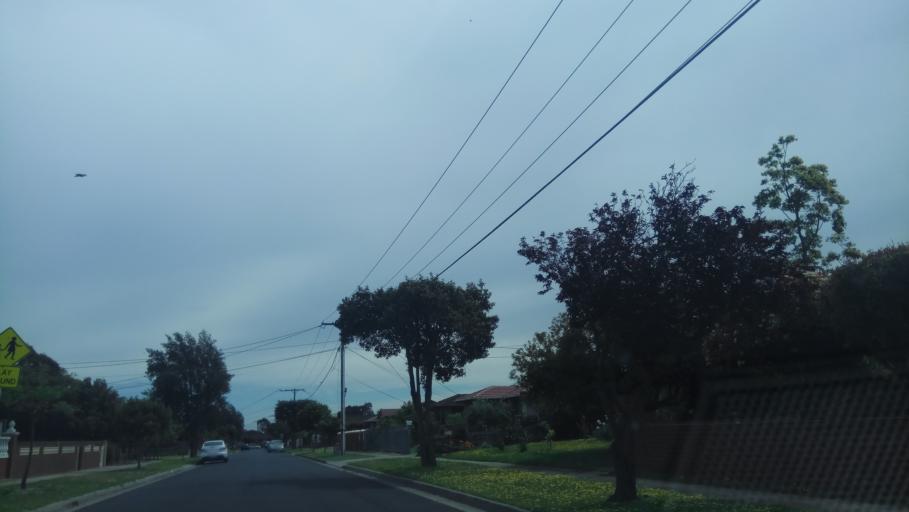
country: AU
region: Victoria
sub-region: Greater Dandenong
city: Springvale South
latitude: -37.9593
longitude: 145.1351
